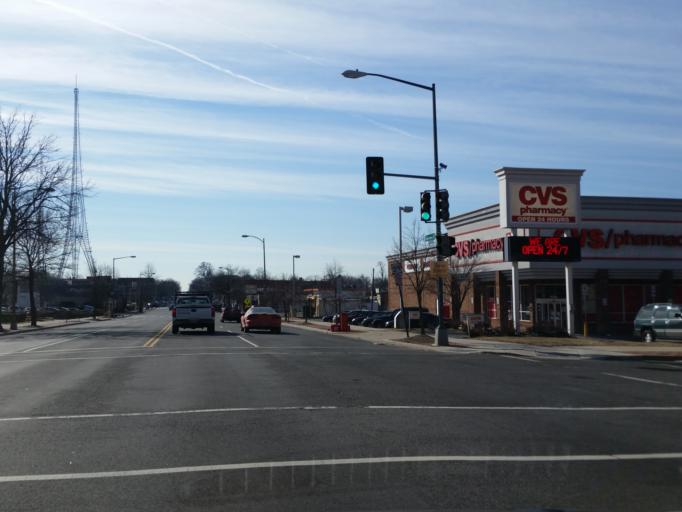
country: US
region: Maryland
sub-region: Montgomery County
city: Silver Spring
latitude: 38.9701
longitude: -77.0273
